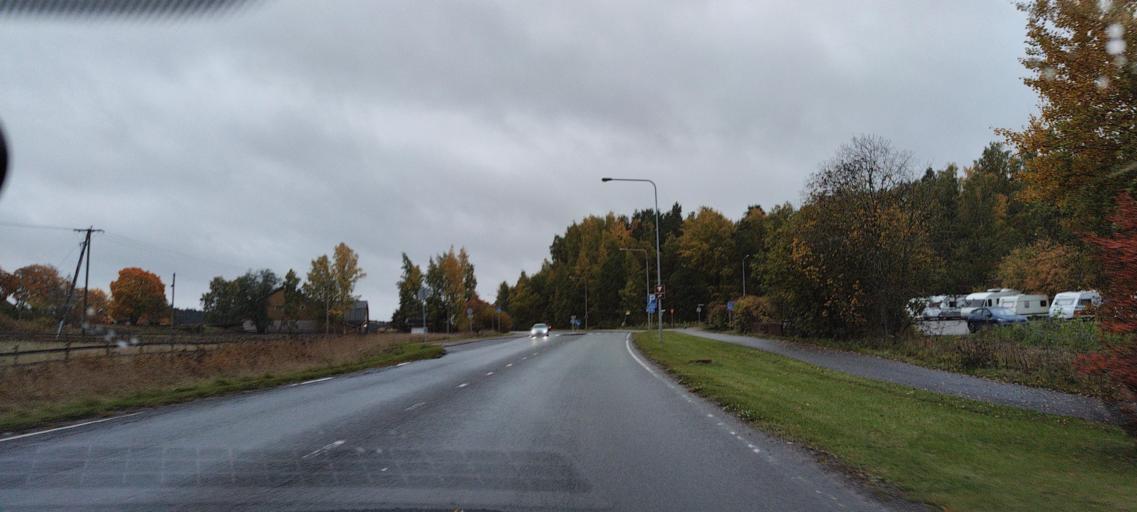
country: FI
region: Varsinais-Suomi
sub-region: Turku
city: Turku
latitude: 60.4628
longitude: 22.3334
